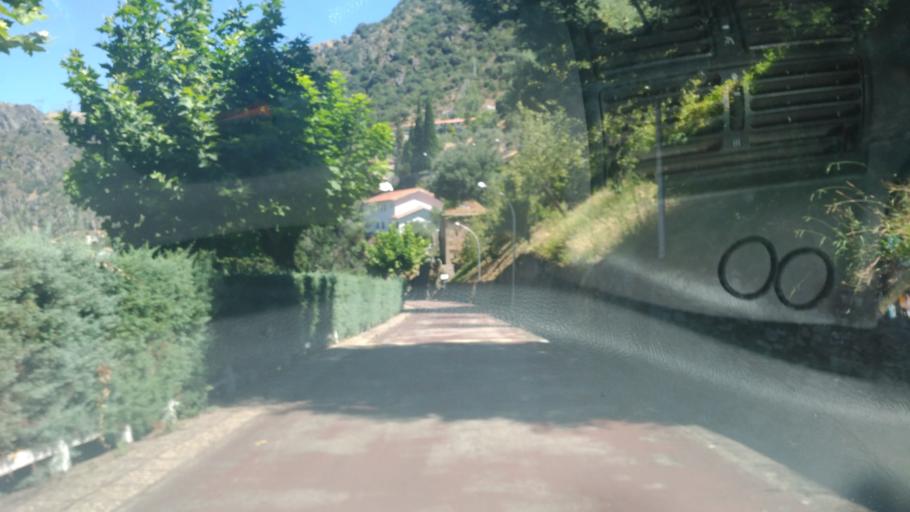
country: ES
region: Castille and Leon
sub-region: Provincia de Salamanca
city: Mieza
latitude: 41.1913
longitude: -6.6903
